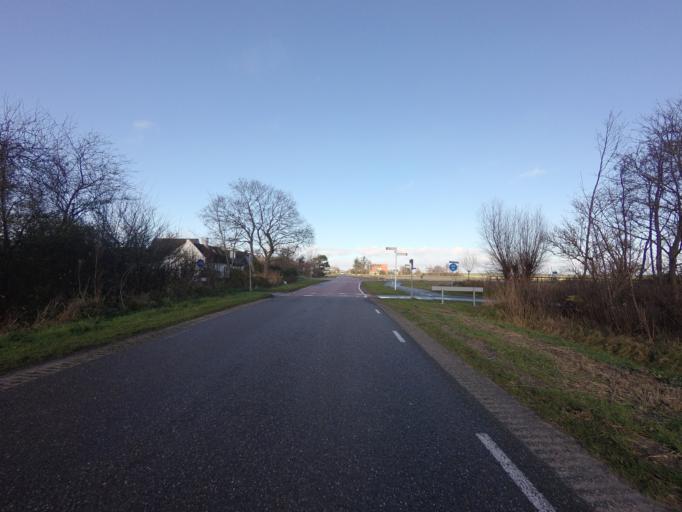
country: NL
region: North Holland
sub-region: Gemeente Texel
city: Den Burg
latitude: 53.1567
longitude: 4.8642
